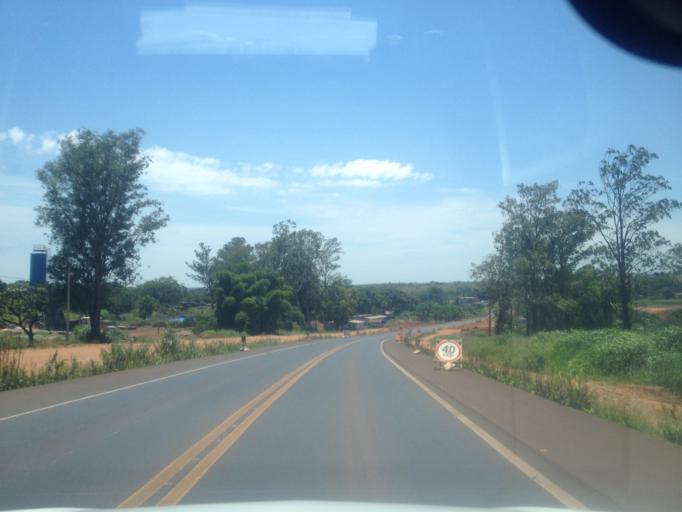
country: BR
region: Minas Gerais
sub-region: Monte Alegre De Minas
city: Monte Alegre de Minas
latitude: -18.8781
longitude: -49.0632
